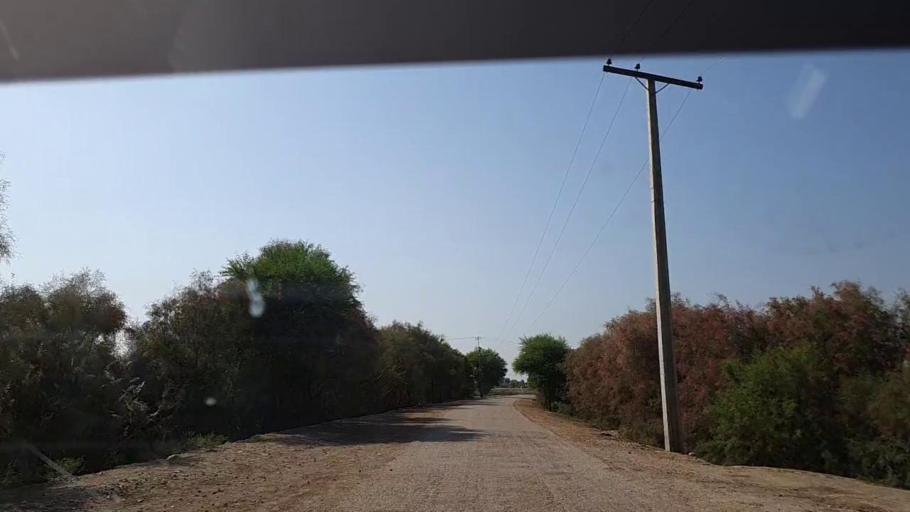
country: PK
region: Sindh
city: Ghauspur
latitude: 28.1974
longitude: 69.0454
